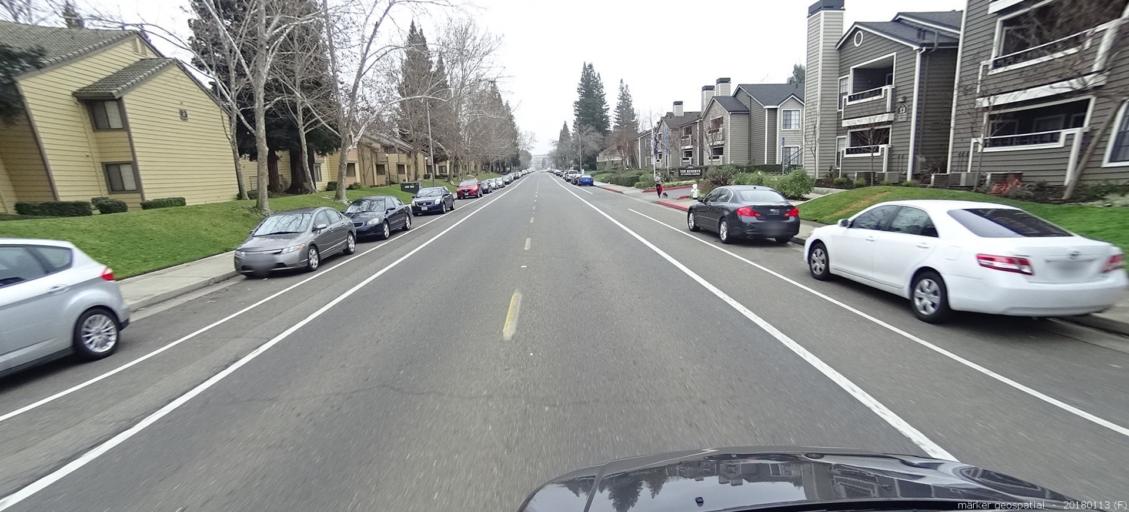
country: US
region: California
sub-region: Sacramento County
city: Rancho Cordova
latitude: 38.5827
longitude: -121.2956
